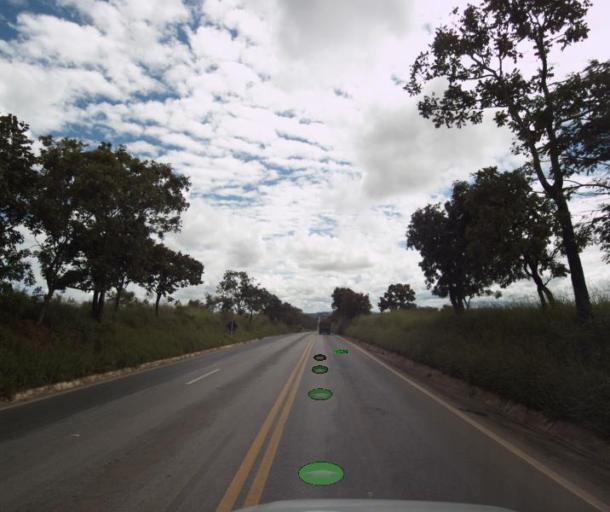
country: BR
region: Goias
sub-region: Uruacu
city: Uruacu
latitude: -14.3871
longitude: -49.1579
